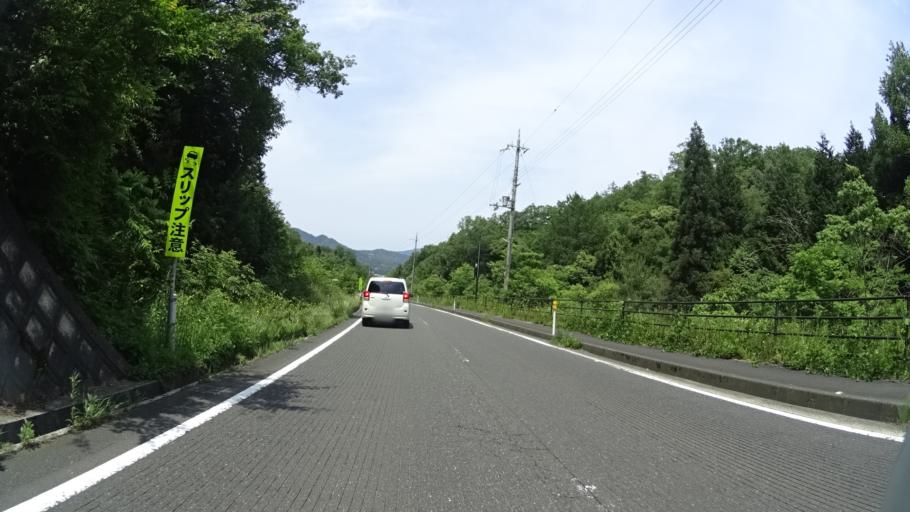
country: JP
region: Kyoto
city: Miyazu
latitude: 35.5827
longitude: 135.1166
